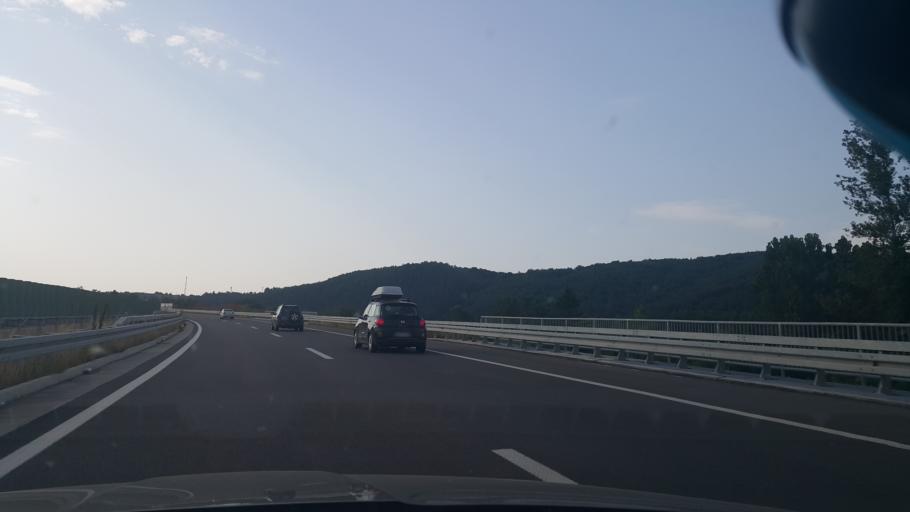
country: RS
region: Central Serbia
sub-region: Jablanicki Okrug
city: Vlasotince
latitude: 42.9082
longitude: 22.0483
